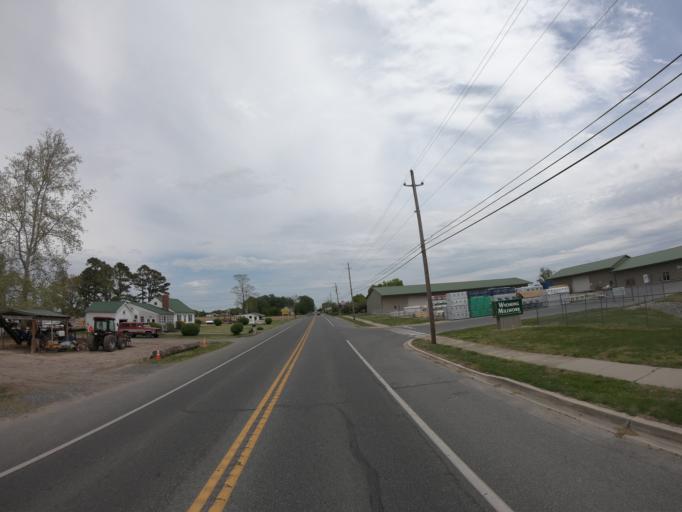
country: US
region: Delaware
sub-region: Sussex County
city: Milton
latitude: 38.7875
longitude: -75.3234
